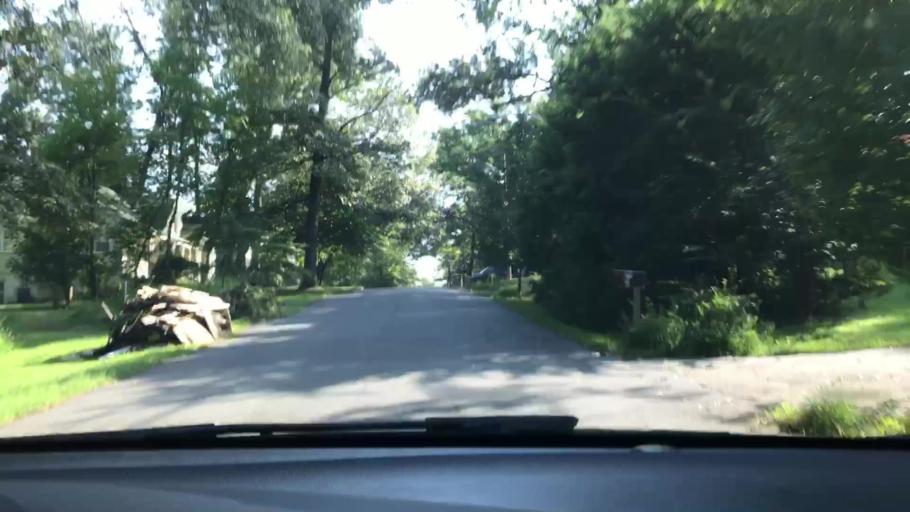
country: US
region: Virginia
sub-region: Fairfax County
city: Annandale
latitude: 38.8496
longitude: -77.2043
